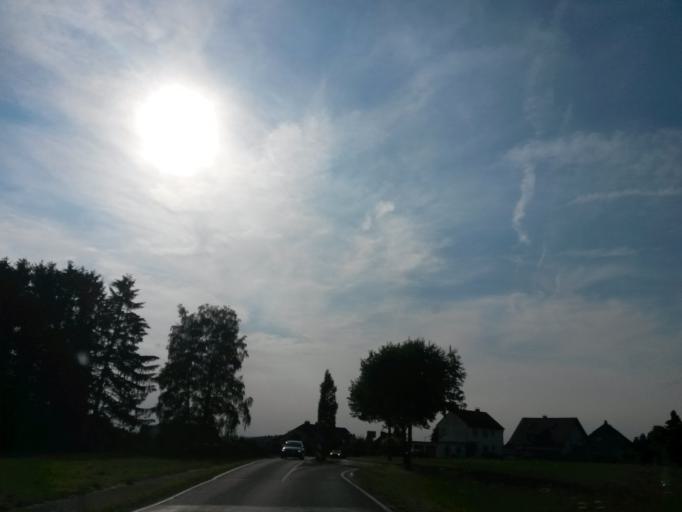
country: DE
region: North Rhine-Westphalia
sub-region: Regierungsbezirk Koln
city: Much
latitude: 50.9411
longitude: 7.3449
